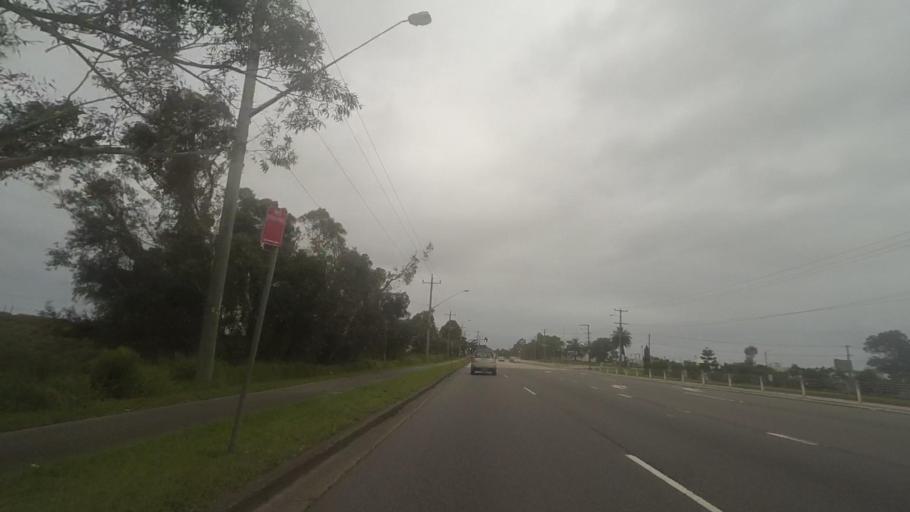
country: AU
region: New South Wales
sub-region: Newcastle
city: Mayfield West
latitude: -32.8696
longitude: 151.7095
